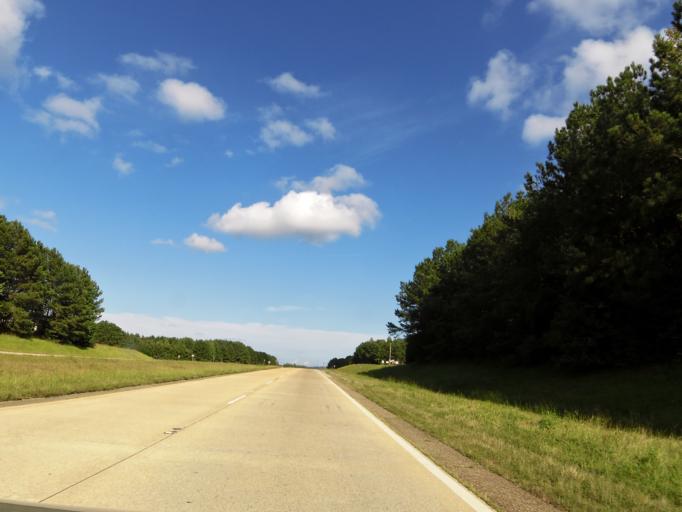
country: US
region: Mississippi
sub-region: Tishomingo County
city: Iuka
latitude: 34.8082
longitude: -88.2718
